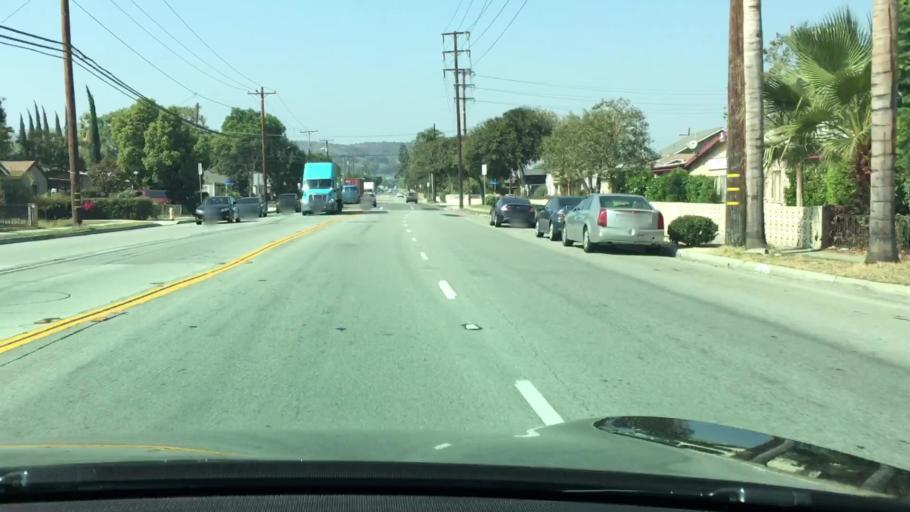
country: US
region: California
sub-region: Los Angeles County
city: Hacienda Heights
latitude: 34.0153
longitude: -117.9765
